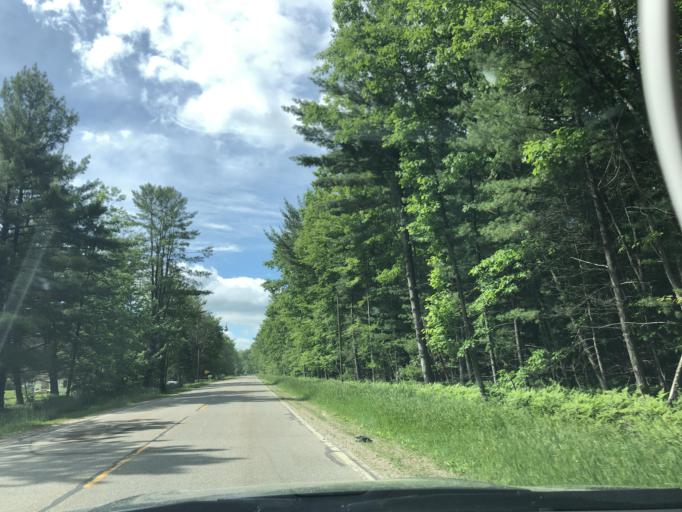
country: US
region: Michigan
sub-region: Roscommon County
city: Houghton Lake
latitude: 44.3564
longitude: -84.8549
